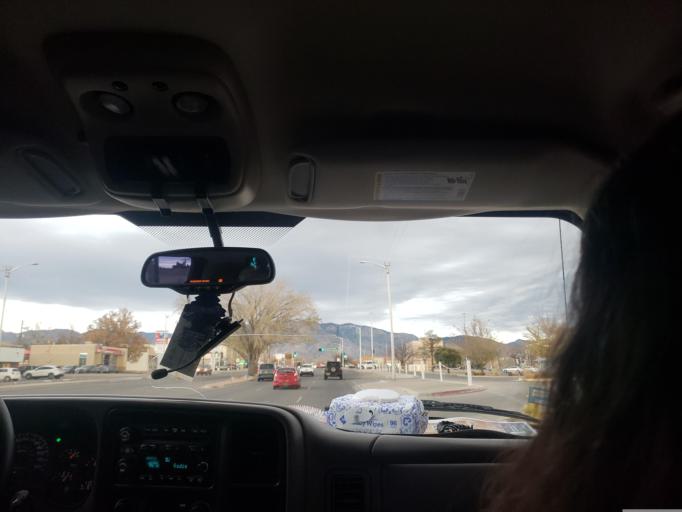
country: US
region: New Mexico
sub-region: Bernalillo County
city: Albuquerque
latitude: 35.1072
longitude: -106.5730
